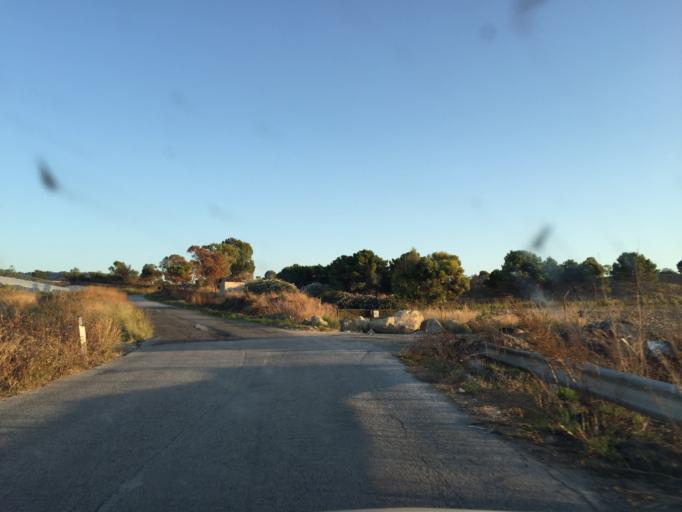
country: IT
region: Calabria
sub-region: Provincia di Vibo-Valentia
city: Pannaconi
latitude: 38.7107
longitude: 16.0490
